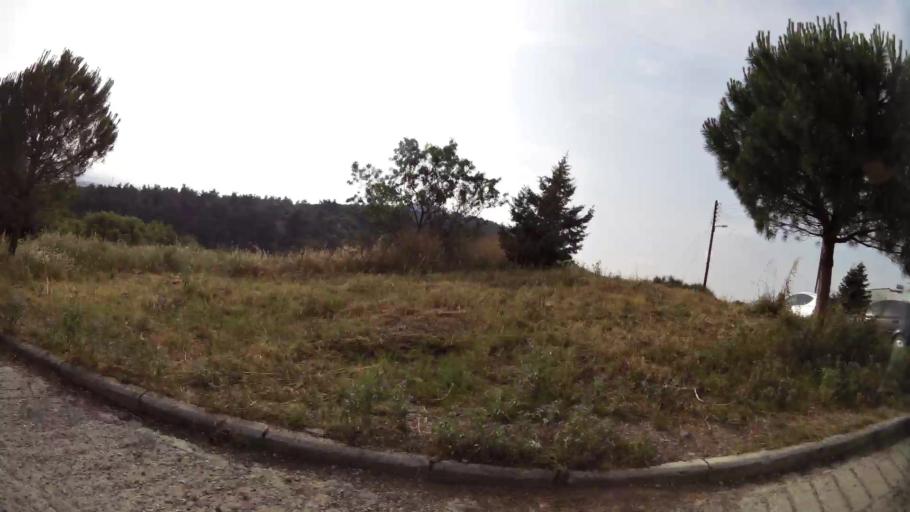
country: GR
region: Central Macedonia
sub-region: Nomos Thessalonikis
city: Oraiokastro
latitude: 40.7254
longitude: 22.9114
